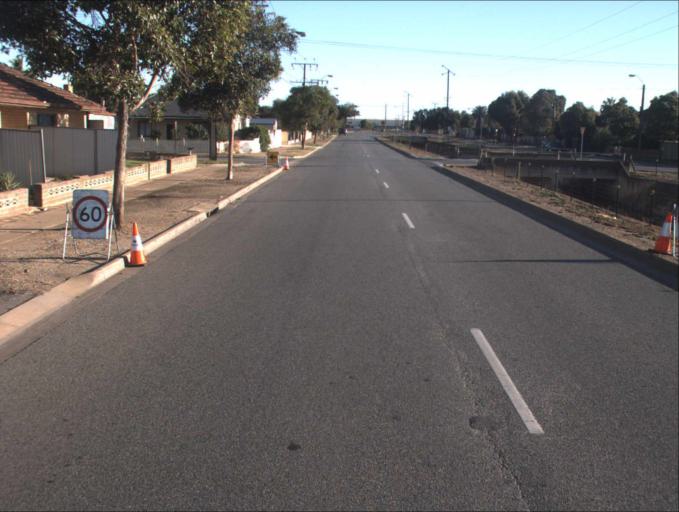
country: AU
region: South Australia
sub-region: Port Adelaide Enfield
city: Alberton
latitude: -34.8458
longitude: 138.5328
